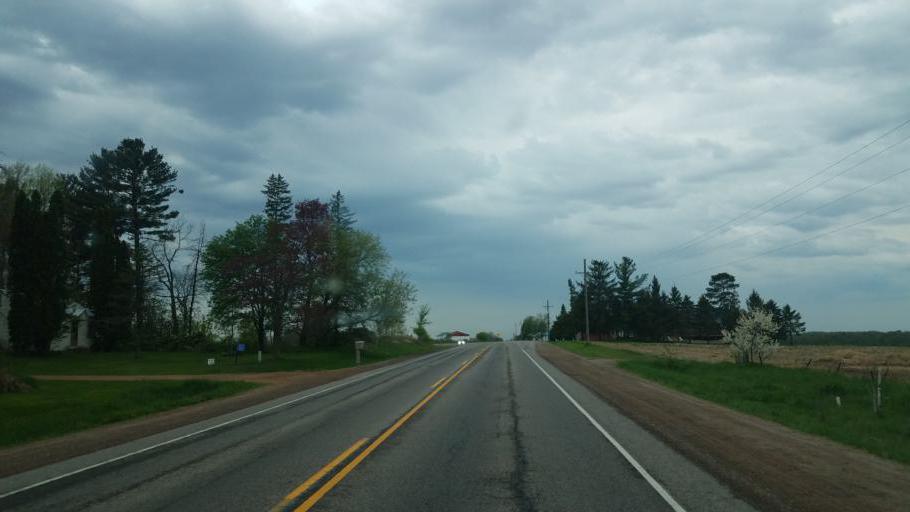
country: US
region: Wisconsin
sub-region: Marathon County
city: Spencer
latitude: 44.5979
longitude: -90.3681
